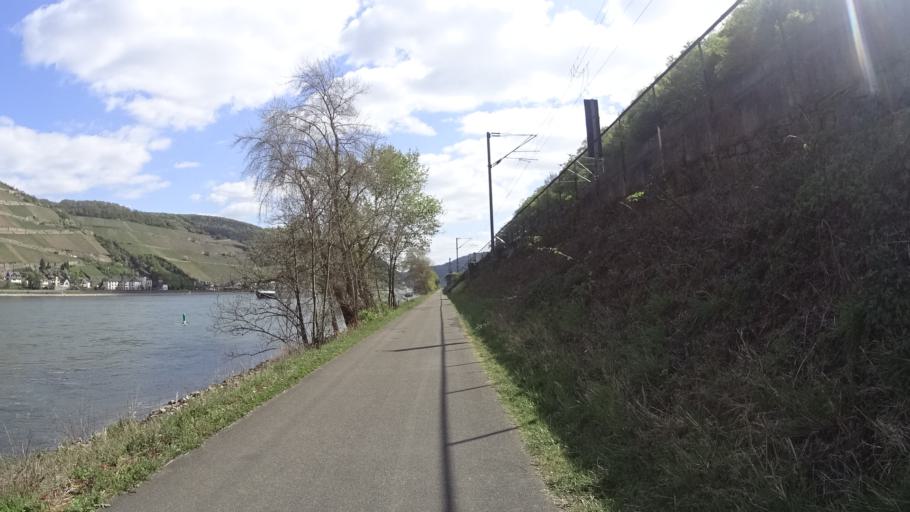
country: DE
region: Rheinland-Pfalz
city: Trechtingshausen
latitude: 49.9978
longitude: 7.8573
